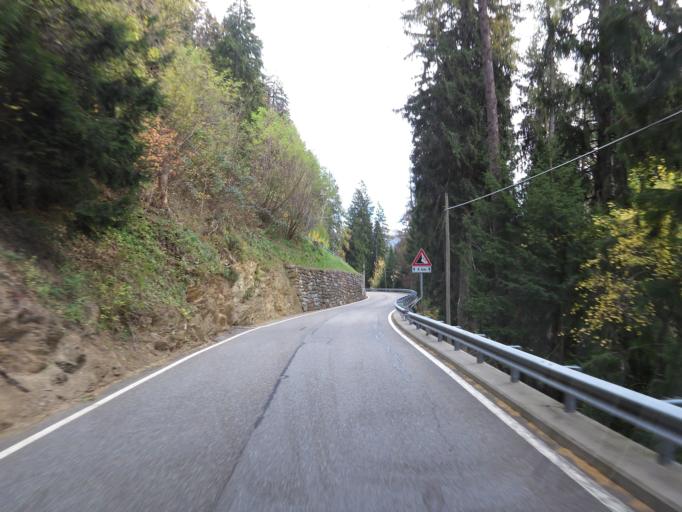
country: IT
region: Trentino-Alto Adige
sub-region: Bolzano
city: San Leonardo in Passiria
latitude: 46.8201
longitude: 11.2524
